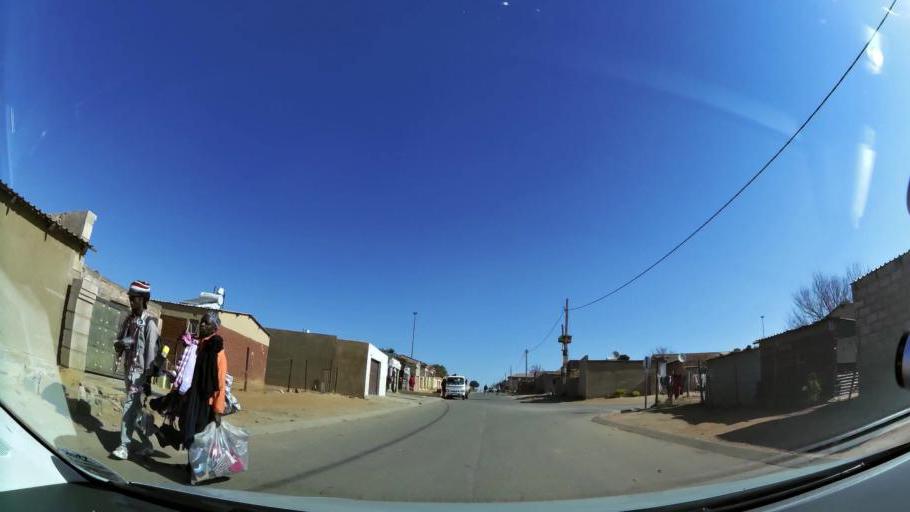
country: ZA
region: Gauteng
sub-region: Ekurhuleni Metropolitan Municipality
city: Tembisa
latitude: -26.0223
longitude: 28.2410
